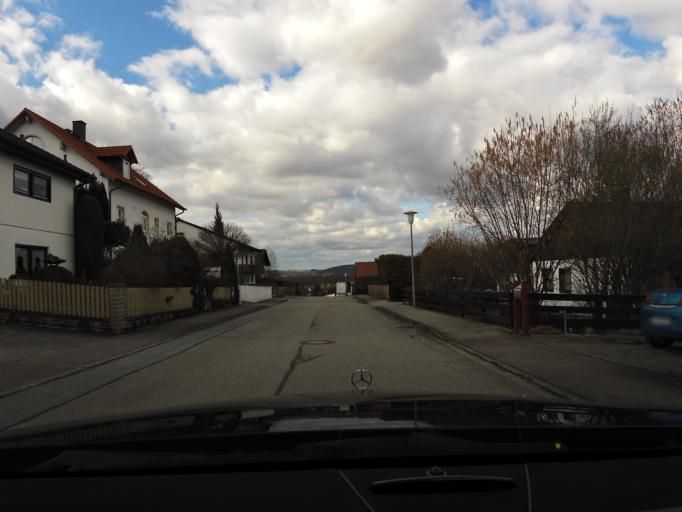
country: DE
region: Bavaria
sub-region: Lower Bavaria
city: Eching
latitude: 48.4954
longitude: 12.0581
